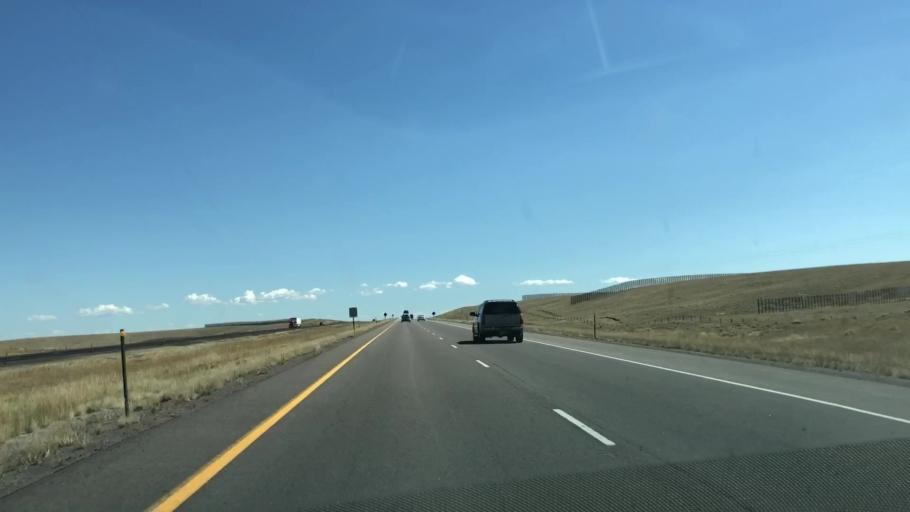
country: US
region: Wyoming
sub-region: Albany County
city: Laramie
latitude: 41.5626
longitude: -106.1231
